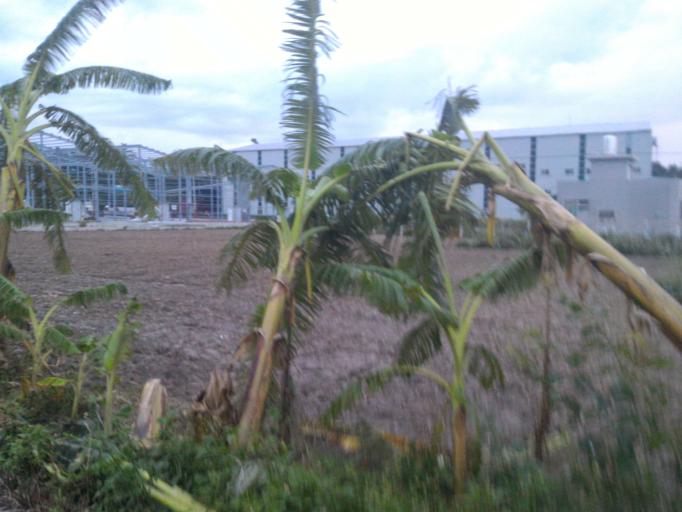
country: TW
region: Taiwan
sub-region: Taoyuan
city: Taoyuan
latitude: 24.9535
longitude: 121.3978
